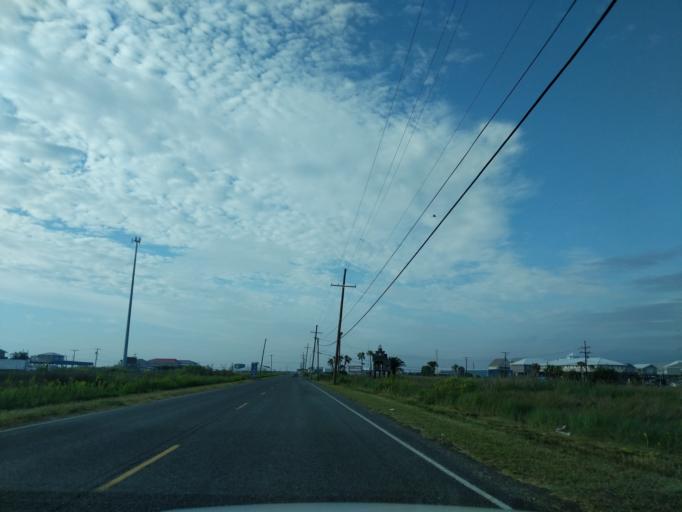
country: US
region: Louisiana
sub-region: Terrebonne Parish
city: Dulac
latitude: 29.2516
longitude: -90.6606
